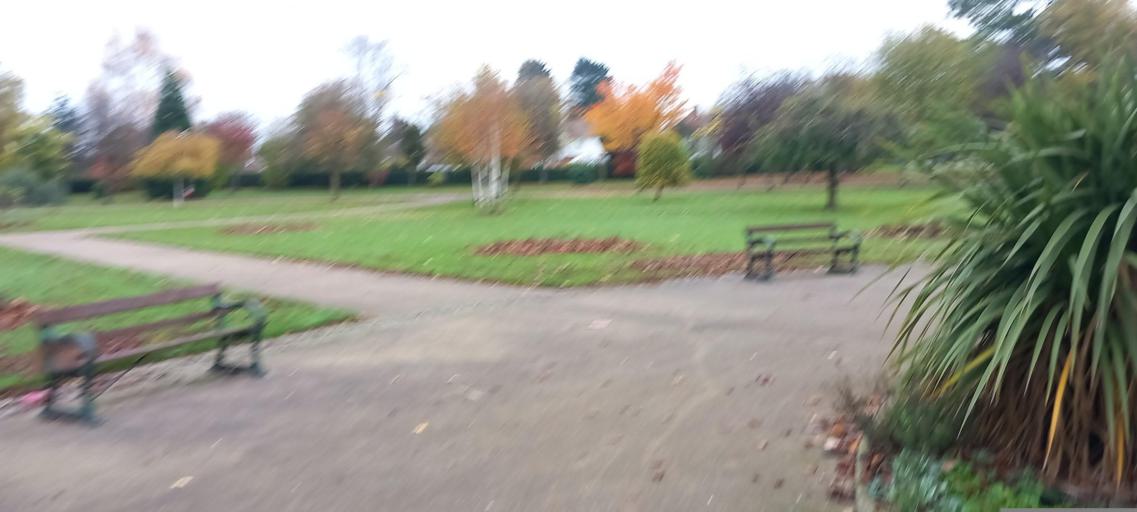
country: GB
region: England
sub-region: East Riding of Yorkshire
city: Airmyn
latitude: 53.7117
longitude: -0.8901
